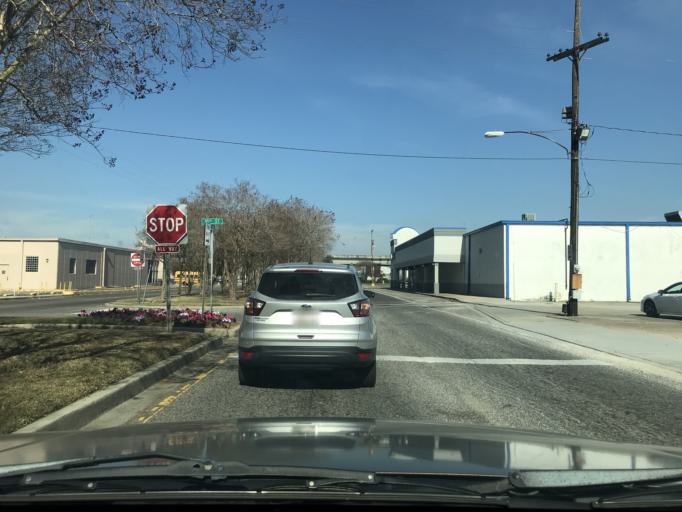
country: US
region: Louisiana
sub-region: Jefferson Parish
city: Marrero
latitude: 29.8937
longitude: -90.0954
